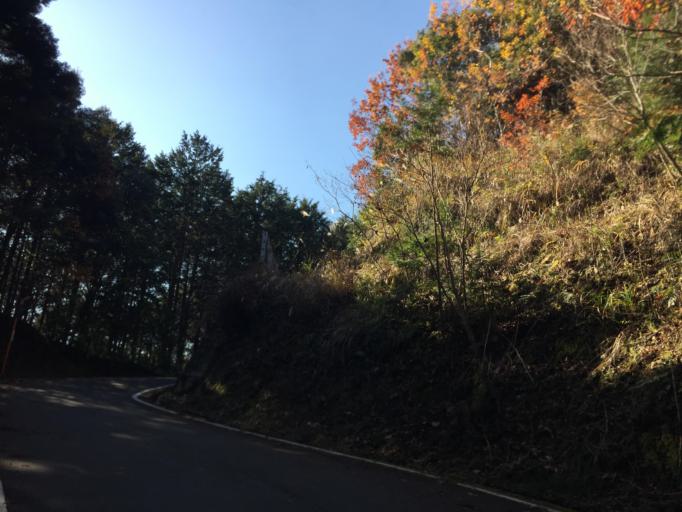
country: JP
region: Wakayama
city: Iwade
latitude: 34.1444
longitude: 135.4113
